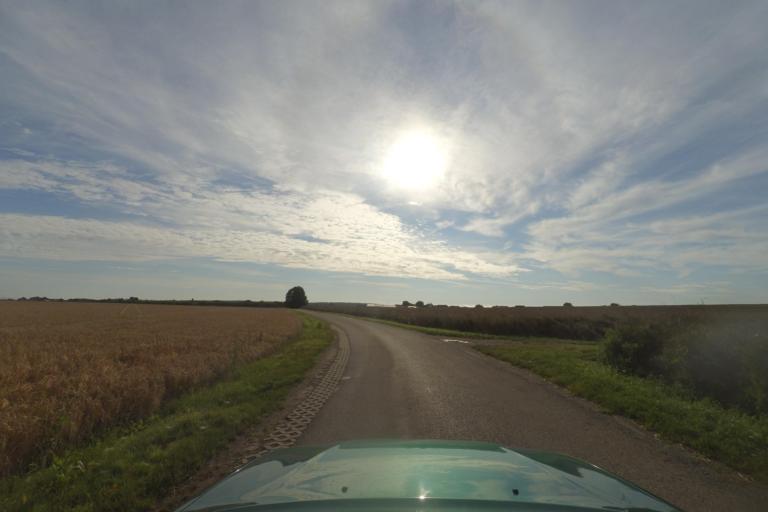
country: DE
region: Bavaria
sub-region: Upper Palatinate
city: Dietfurt
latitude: 48.9900
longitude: 11.5198
